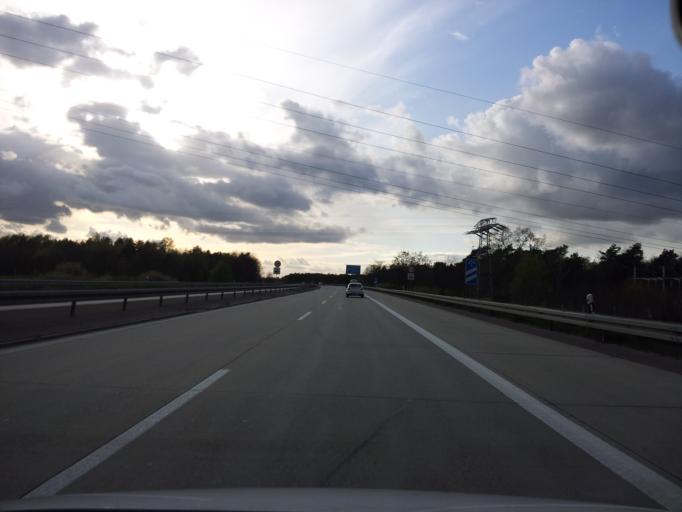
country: DE
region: Brandenburg
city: Cottbus
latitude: 51.7231
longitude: 14.3058
